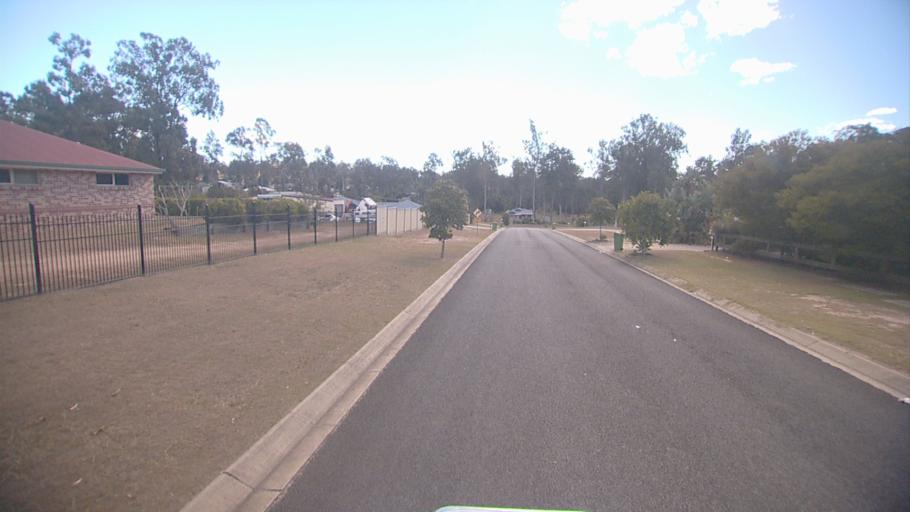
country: AU
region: Queensland
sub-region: Logan
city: North Maclean
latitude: -27.7505
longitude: 152.9403
